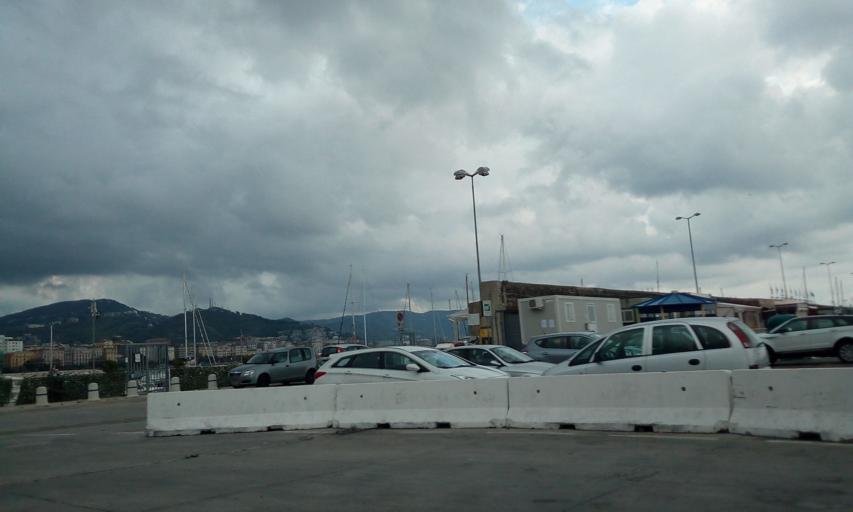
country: IT
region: Campania
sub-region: Provincia di Salerno
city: Vietri sul Mare
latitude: 40.6738
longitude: 14.7525
